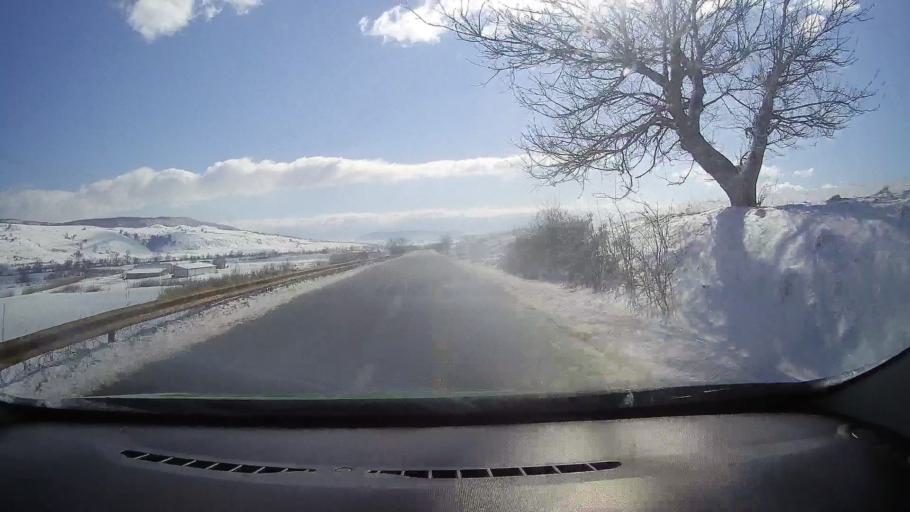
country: RO
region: Sibiu
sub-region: Comuna Rosia
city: Rosia
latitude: 45.8326
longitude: 24.3109
